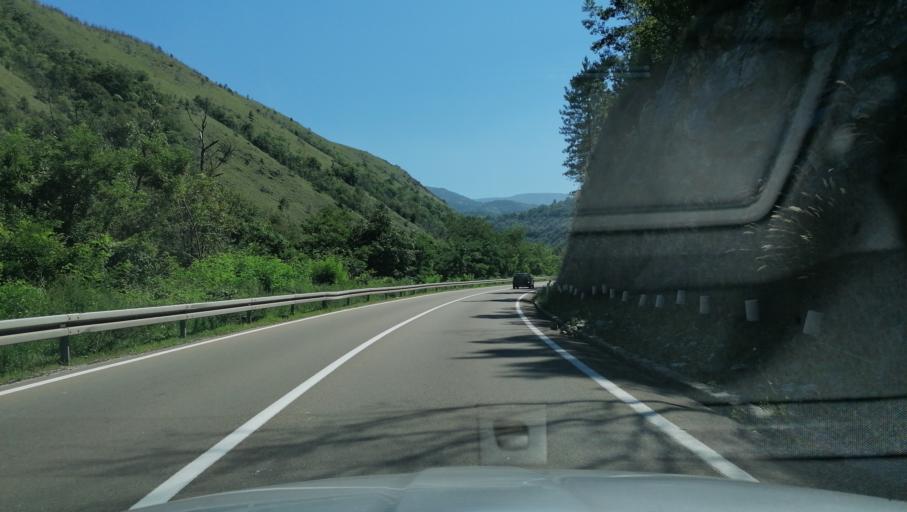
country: RS
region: Central Serbia
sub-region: Raski Okrug
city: Kraljevo
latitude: 43.5679
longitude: 20.6008
